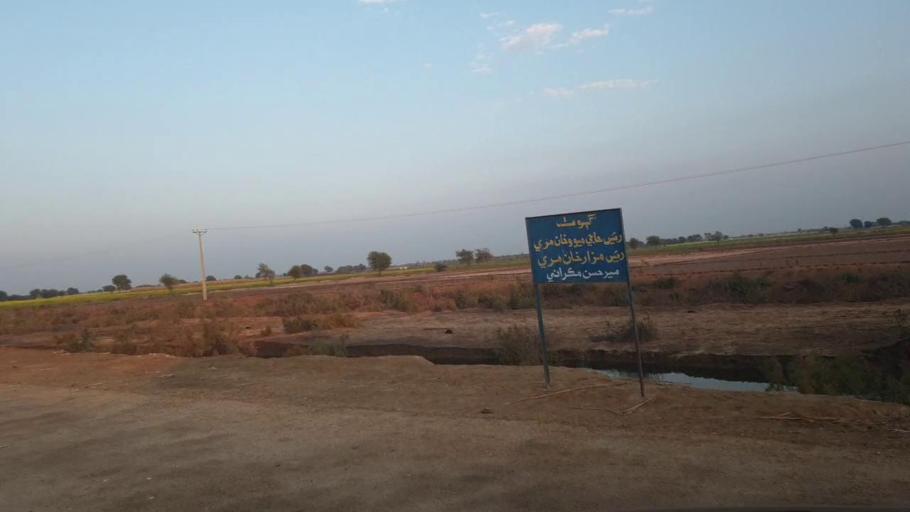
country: PK
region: Sindh
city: Berani
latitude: 25.8262
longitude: 68.7458
